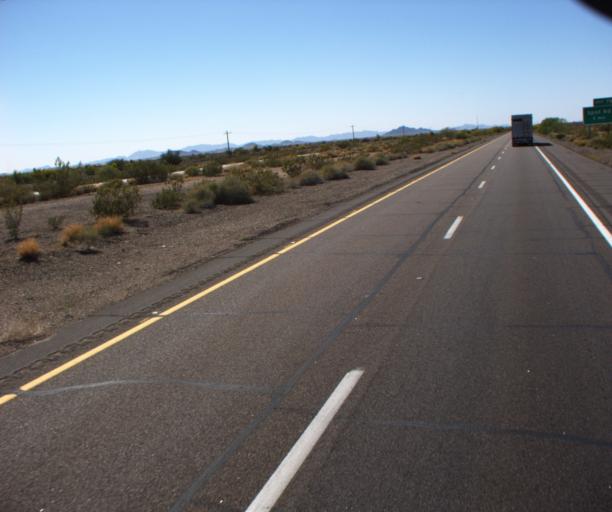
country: US
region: Arizona
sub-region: Maricopa County
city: Gila Bend
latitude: 32.8385
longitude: -113.3362
